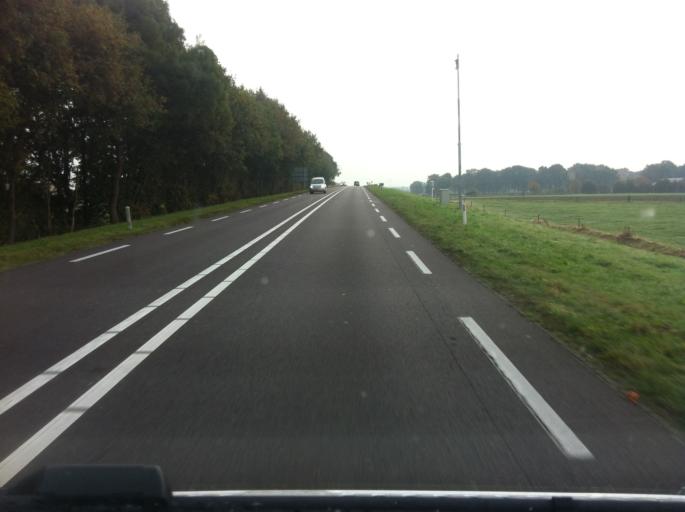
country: NL
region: Overijssel
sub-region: Gemeente Wierden
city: Wierden
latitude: 52.3575
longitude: 6.5703
